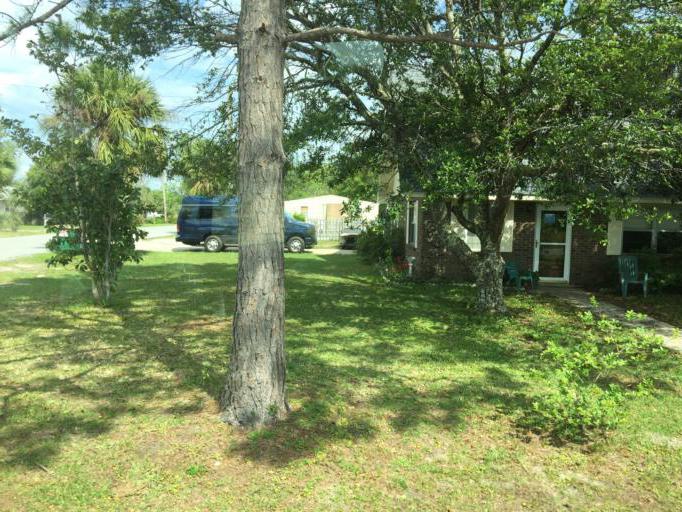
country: US
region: Florida
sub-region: Bay County
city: Laguna Beach
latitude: 30.2234
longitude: -85.8855
